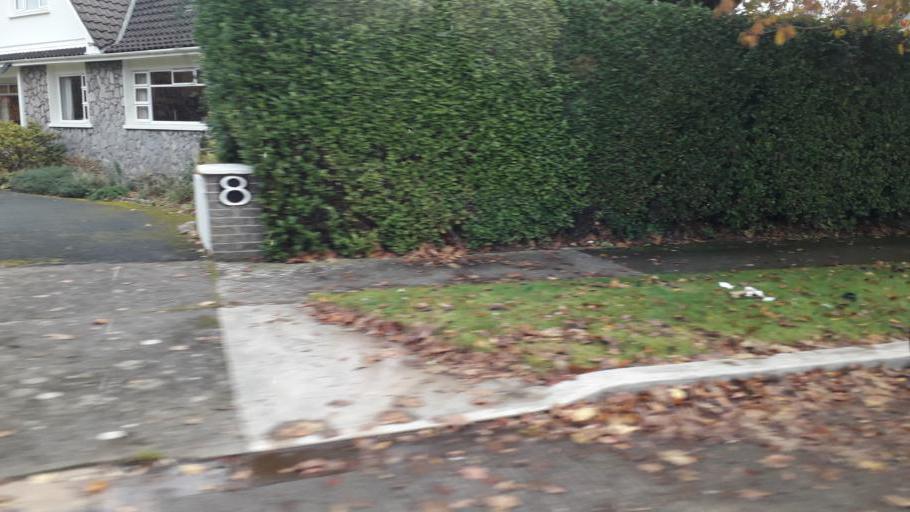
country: IE
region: Leinster
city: Mount Merrion
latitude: 53.2988
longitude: -6.2293
